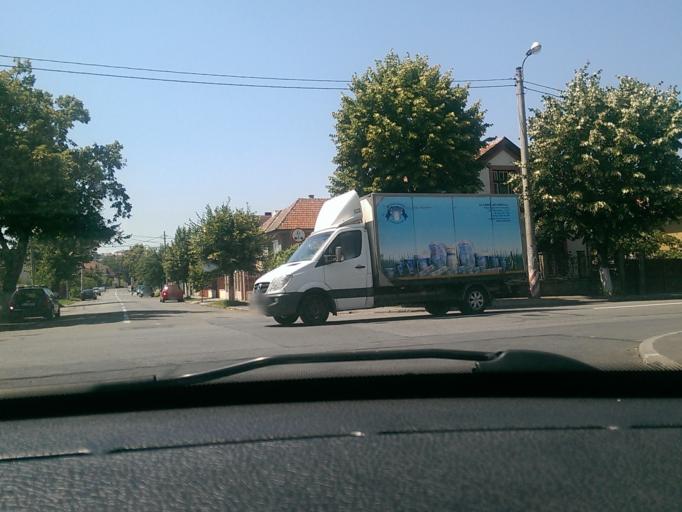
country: RO
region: Cluj
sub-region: Municipiul Cluj-Napoca
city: Cluj-Napoca
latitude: 46.7630
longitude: 23.6096
